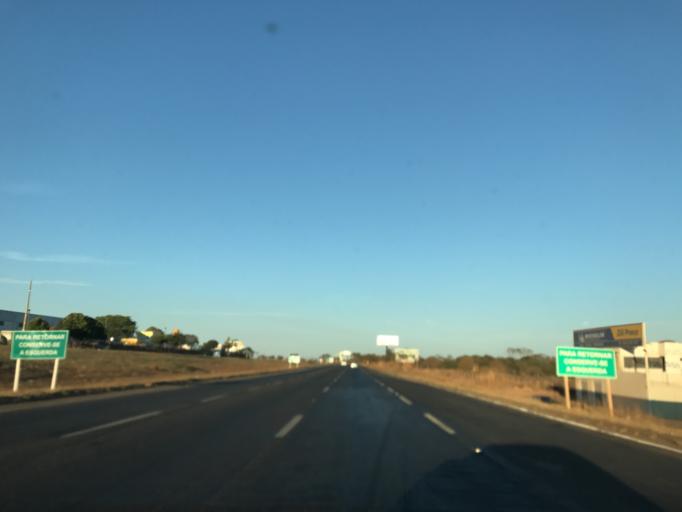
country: BR
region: Goias
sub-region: Anapolis
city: Anapolis
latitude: -16.4033
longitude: -48.9783
